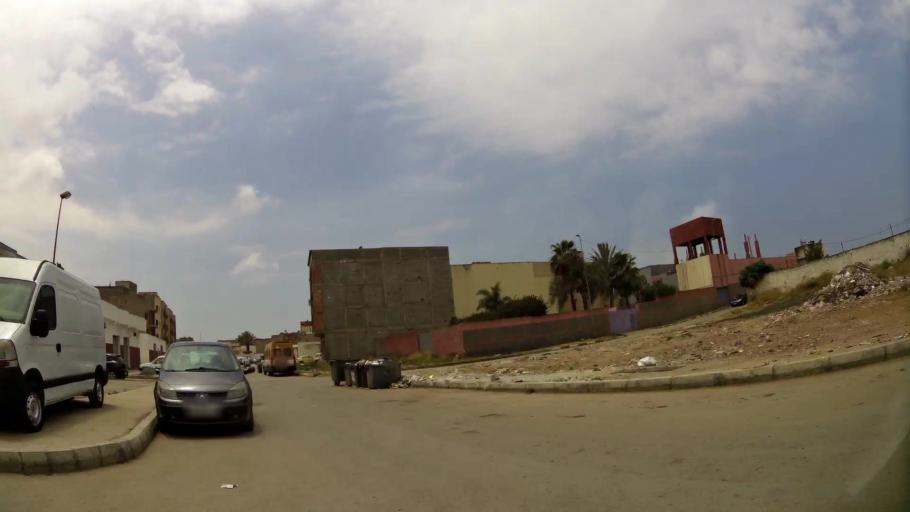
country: MA
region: Rabat-Sale-Zemmour-Zaer
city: Sale
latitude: 34.0550
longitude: -6.7868
